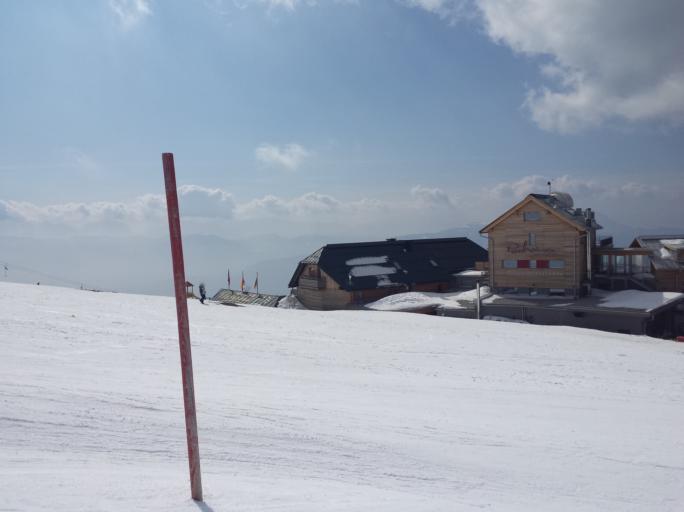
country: AT
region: Carinthia
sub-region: Politischer Bezirk Villach Land
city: Arriach
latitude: 46.6960
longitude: 13.9121
